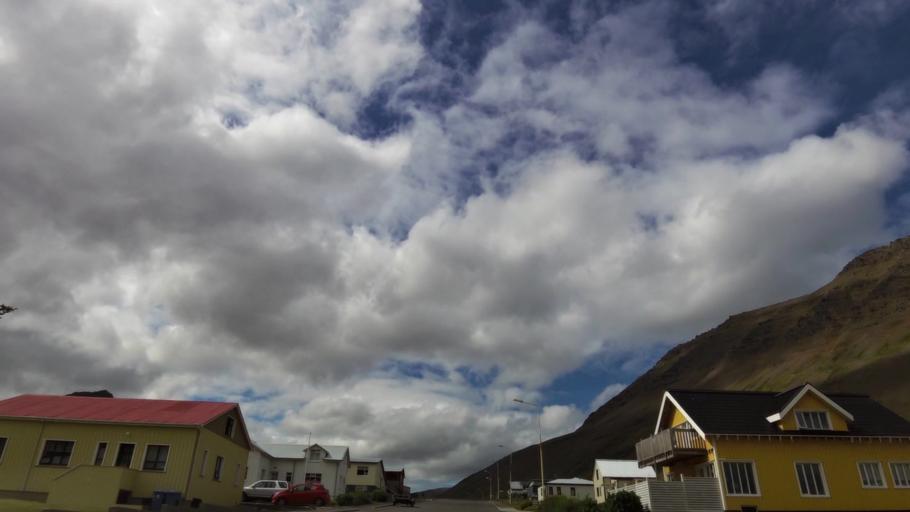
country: IS
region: Westfjords
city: Isafjoerdur
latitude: 66.1577
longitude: -23.2562
